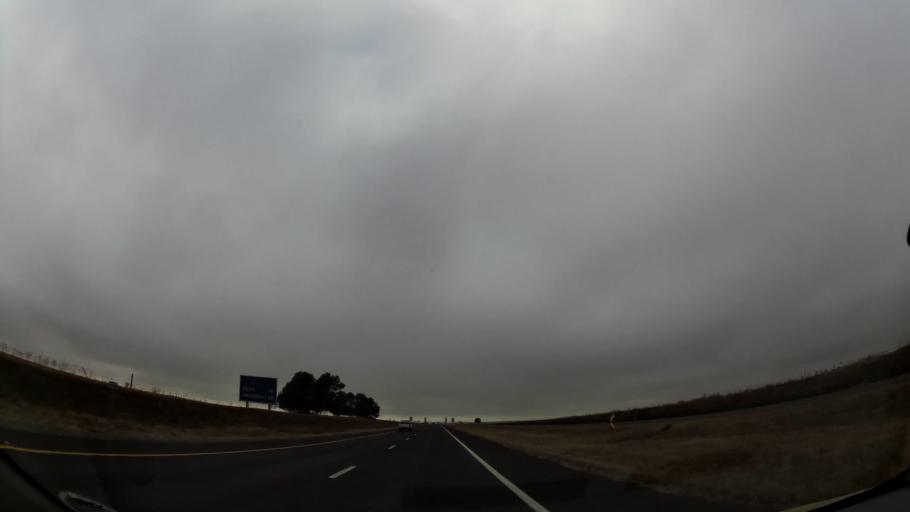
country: ZA
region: Mpumalanga
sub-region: Nkangala District Municipality
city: Delmas
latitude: -26.0693
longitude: 28.7656
